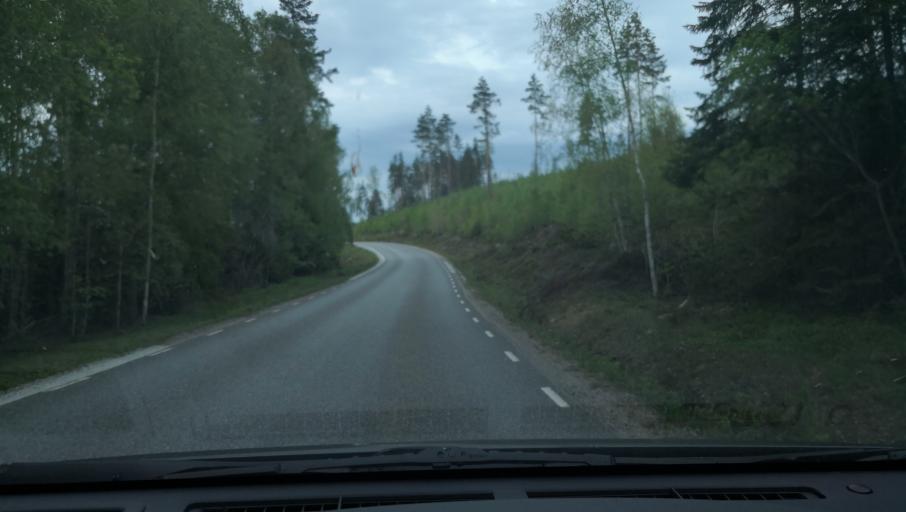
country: SE
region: Vaestmanland
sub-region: Skinnskattebergs Kommun
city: Skinnskatteberg
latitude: 59.8247
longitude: 15.5811
